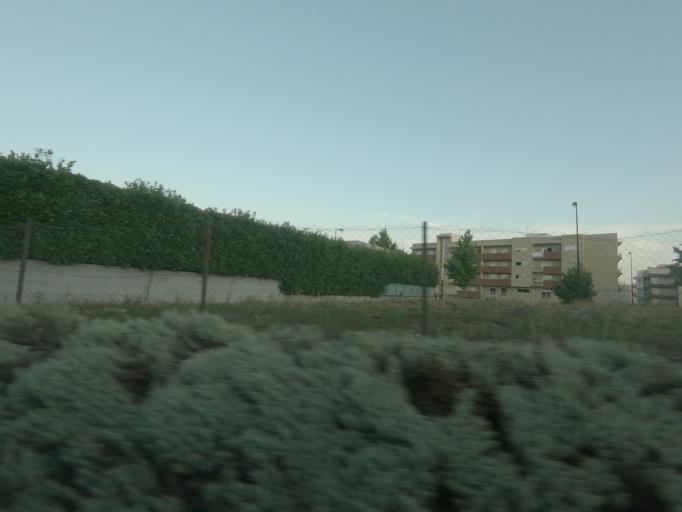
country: PT
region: Vila Real
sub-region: Vila Real
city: Vila Real
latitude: 41.3093
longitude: -7.7385
